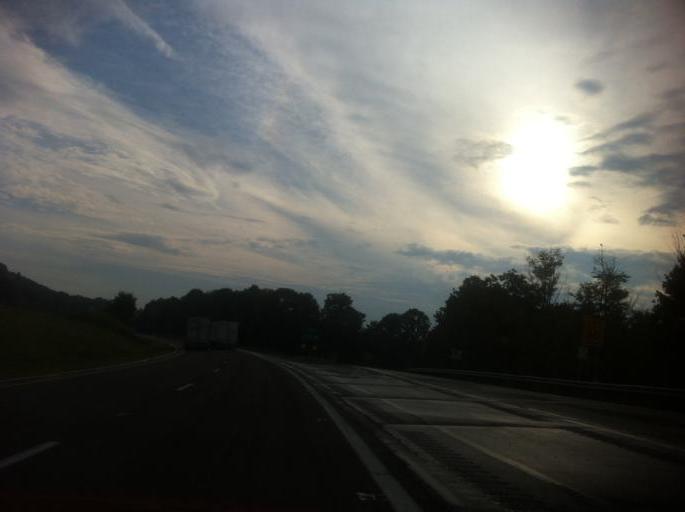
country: US
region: Pennsylvania
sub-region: Clarion County
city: Knox
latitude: 41.1860
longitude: -79.6698
